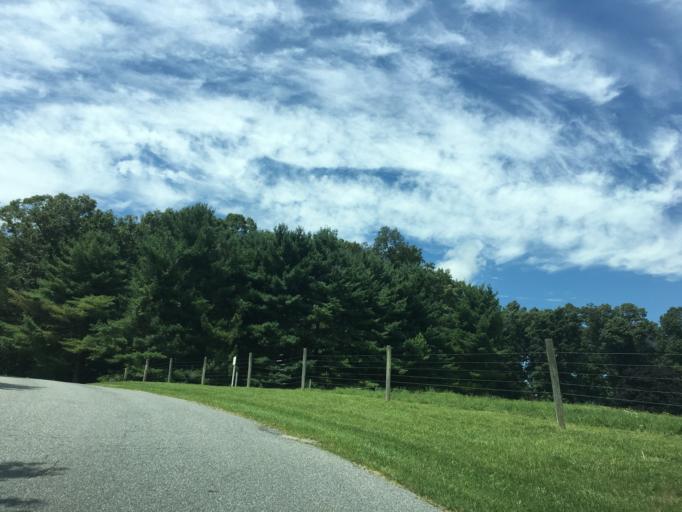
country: US
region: Pennsylvania
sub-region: York County
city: New Freedom
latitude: 39.6958
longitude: -76.6937
